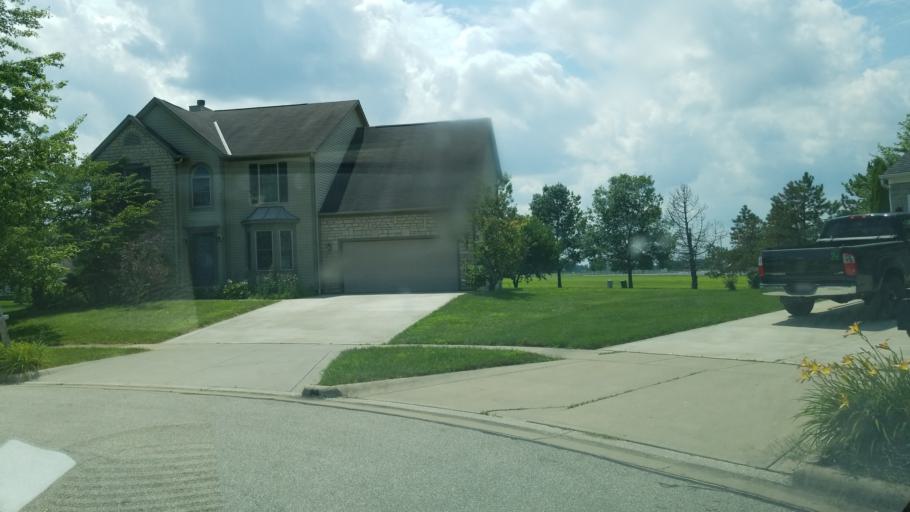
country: US
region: Ohio
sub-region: Delaware County
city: Lewis Center
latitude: 40.2189
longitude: -82.9985
